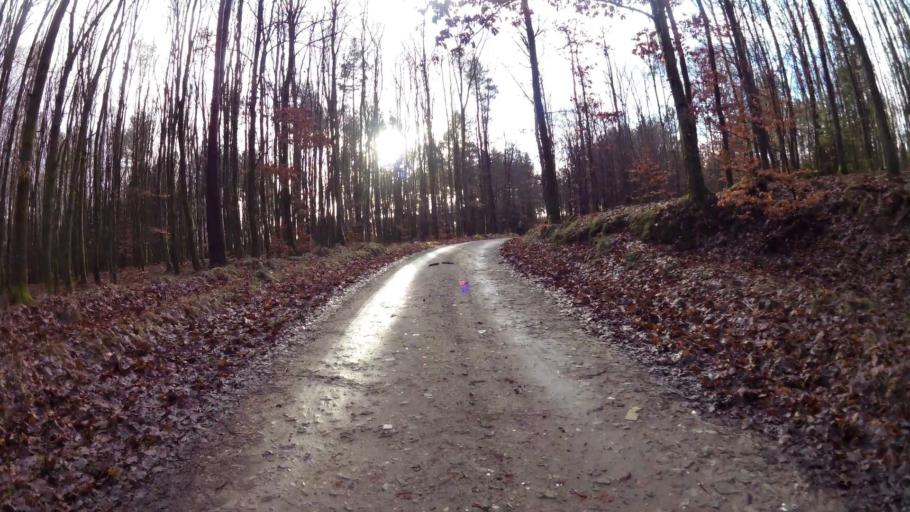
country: PL
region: West Pomeranian Voivodeship
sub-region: Powiat koszalinski
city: Sianow
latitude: 54.1118
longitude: 16.2990
